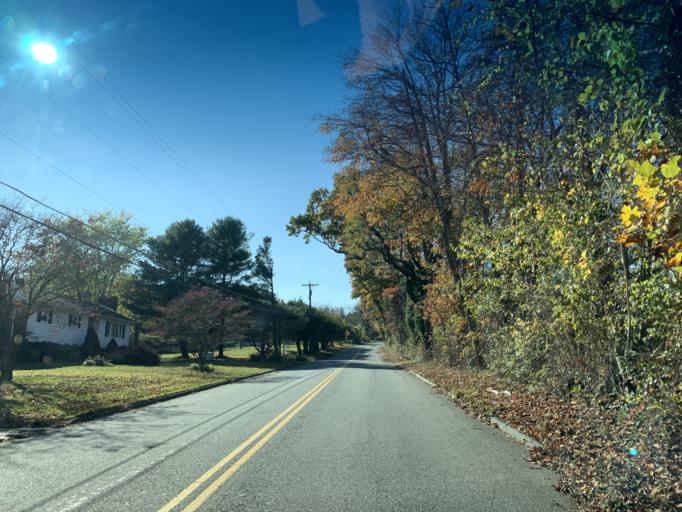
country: US
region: Maryland
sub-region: Harford County
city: Joppatowne
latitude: 39.4722
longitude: -76.3704
